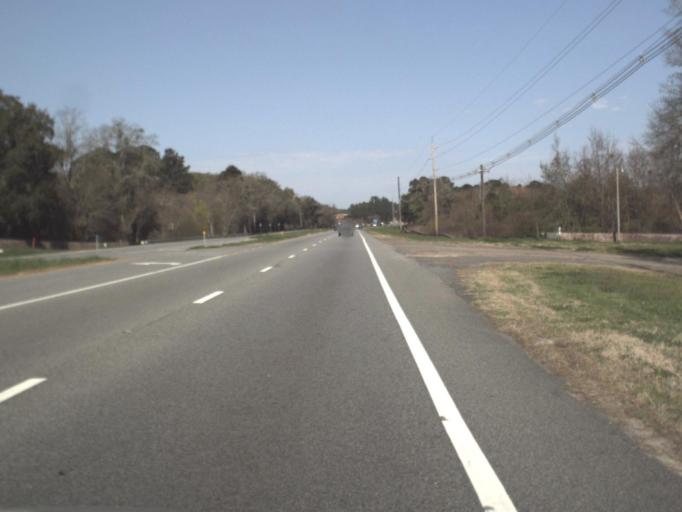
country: US
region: Florida
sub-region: Gadsden County
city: Midway
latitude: 30.5230
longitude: -84.3528
